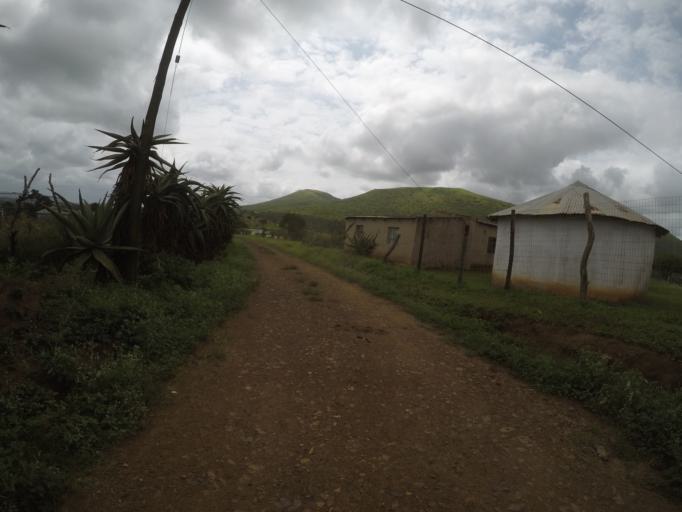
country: ZA
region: KwaZulu-Natal
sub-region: uThungulu District Municipality
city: Empangeni
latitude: -28.5841
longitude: 31.8655
